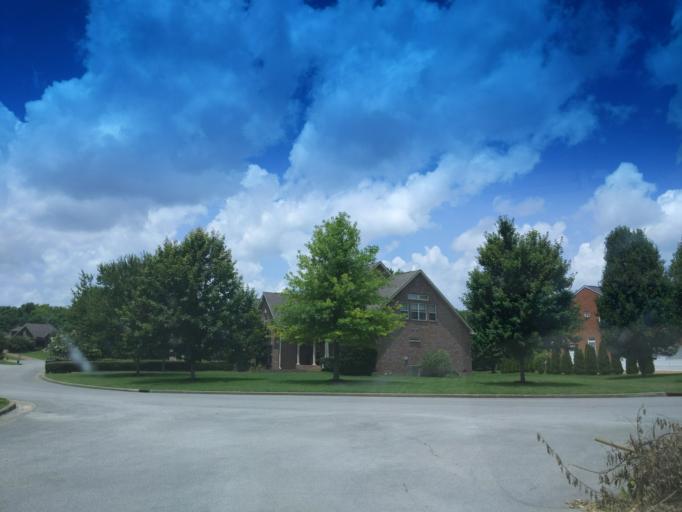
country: US
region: Tennessee
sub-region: Williamson County
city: Brentwood Estates
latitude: 36.0095
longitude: -86.7819
